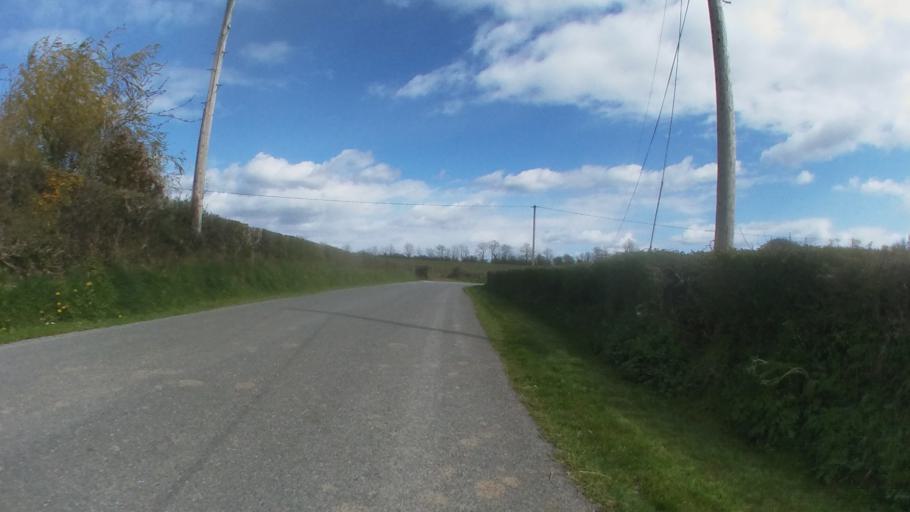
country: IE
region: Leinster
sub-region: Kilkenny
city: Kilkenny
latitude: 52.7150
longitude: -7.2239
